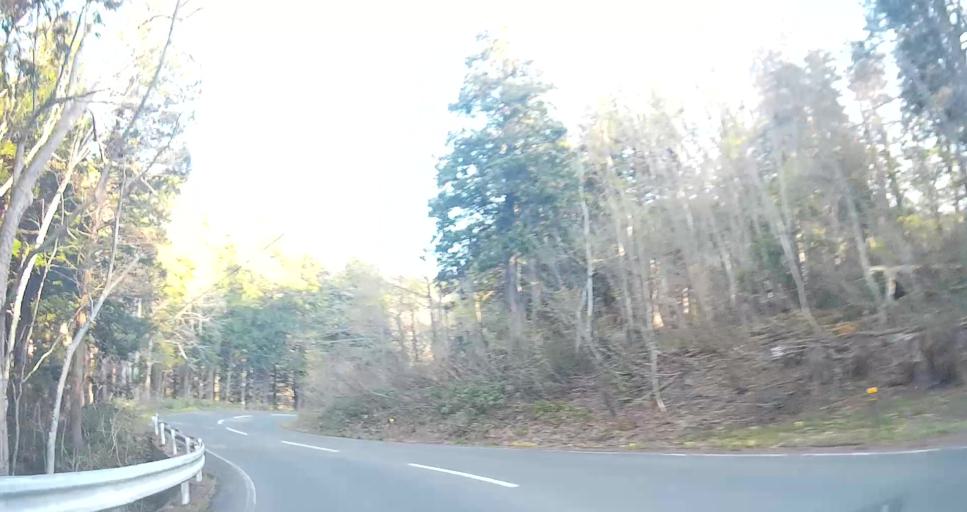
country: JP
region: Aomori
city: Mutsu
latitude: 41.3156
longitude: 141.1123
